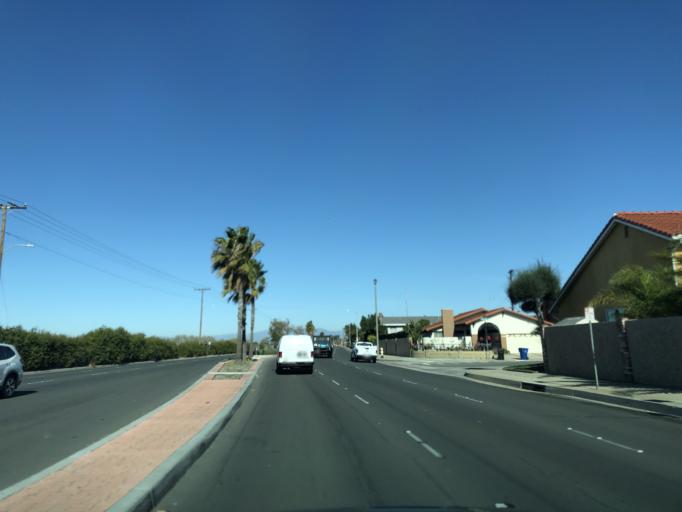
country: US
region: California
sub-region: Orange County
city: Westminster
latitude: 33.7600
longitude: -118.0425
